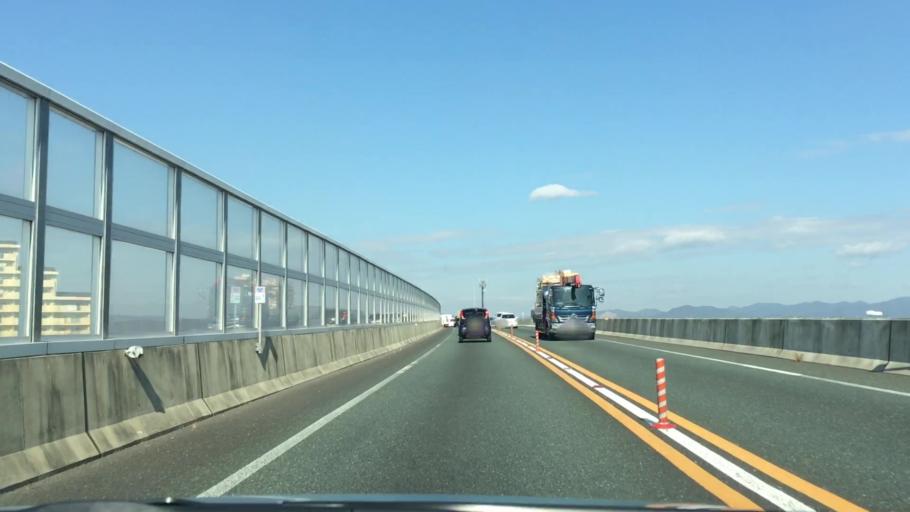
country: JP
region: Aichi
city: Kozakai-cho
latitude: 34.7831
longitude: 137.3329
